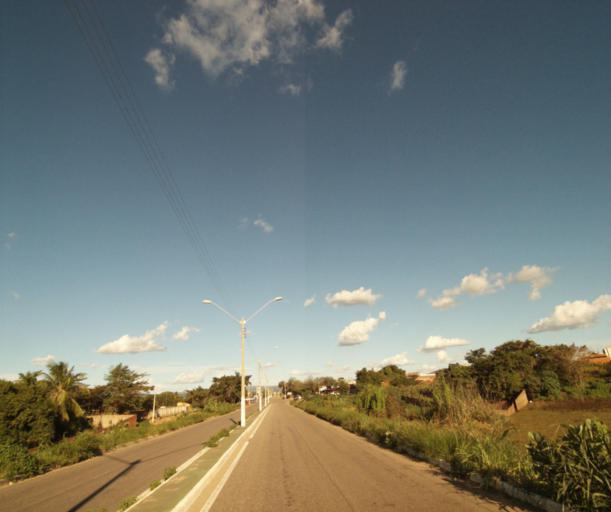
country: BR
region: Bahia
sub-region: Guanambi
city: Guanambi
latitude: -14.2109
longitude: -42.7933
